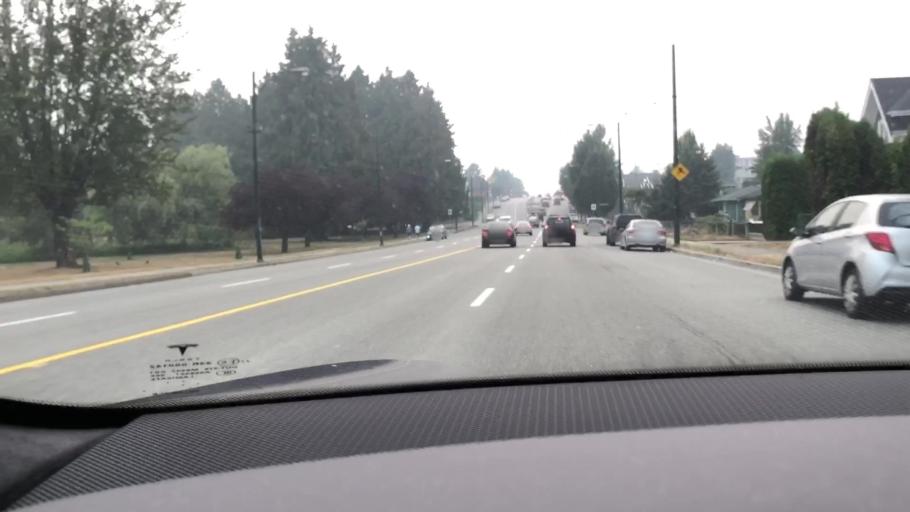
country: CA
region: British Columbia
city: Vancouver
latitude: 49.2328
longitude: -123.0855
